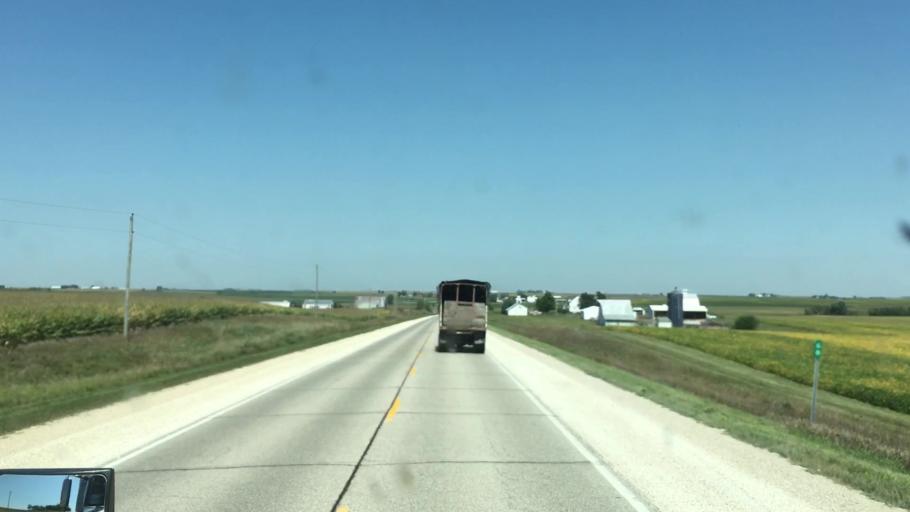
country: US
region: Iowa
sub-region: Tama County
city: Dysart
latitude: 42.0587
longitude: -92.2987
